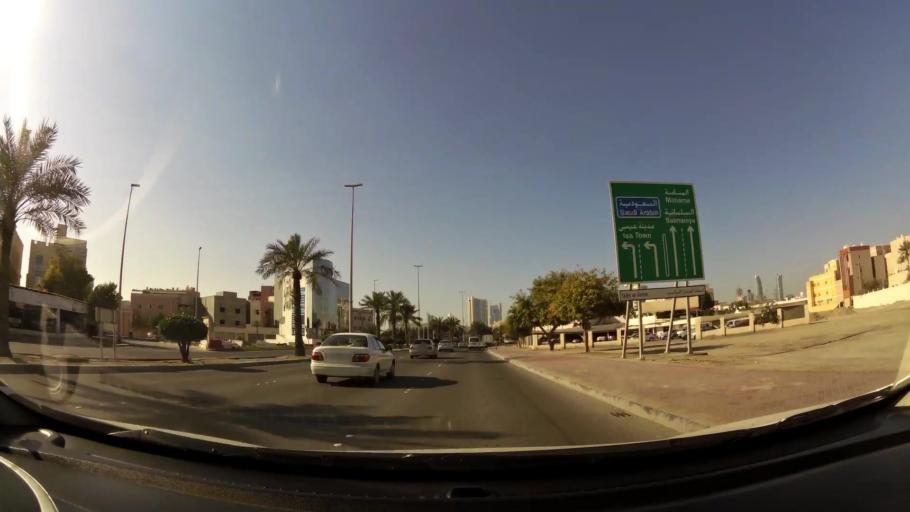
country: BH
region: Manama
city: Manama
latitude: 26.2142
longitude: 50.5657
